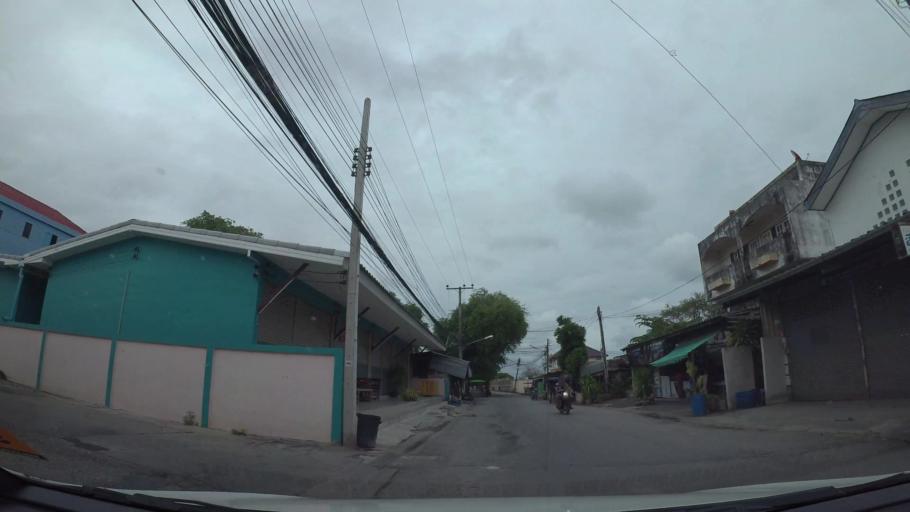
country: TH
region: Rayong
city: Rayong
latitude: 12.6600
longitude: 101.2759
